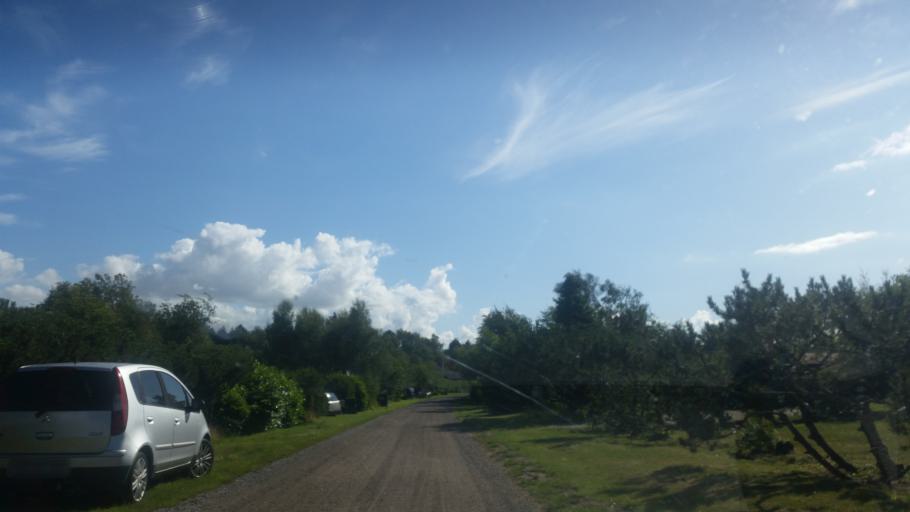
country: DK
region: Zealand
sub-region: Odsherred Kommune
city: Horve
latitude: 55.8114
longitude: 11.4108
